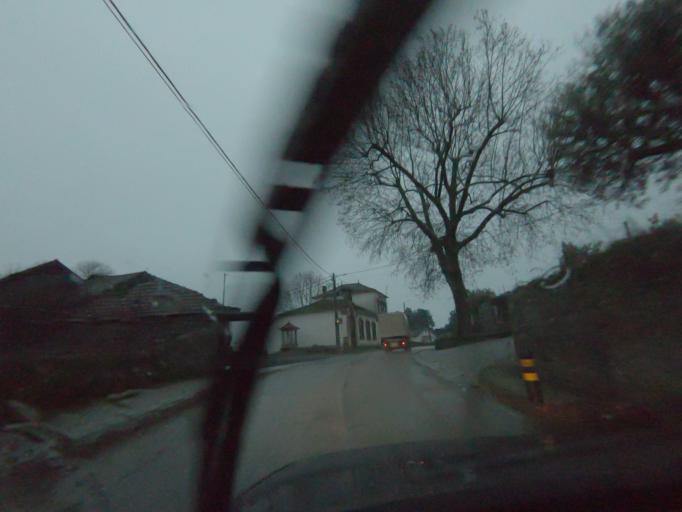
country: PT
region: Vila Real
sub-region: Sabrosa
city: Sabrosa
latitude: 41.2461
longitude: -7.5750
